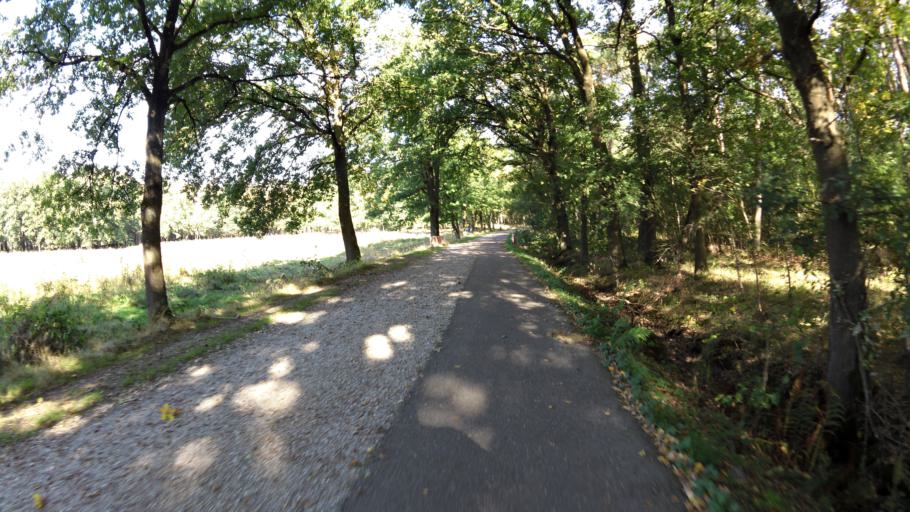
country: DE
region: North Rhine-Westphalia
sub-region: Regierungsbezirk Koln
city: Gangelt
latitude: 50.9768
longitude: 6.0079
